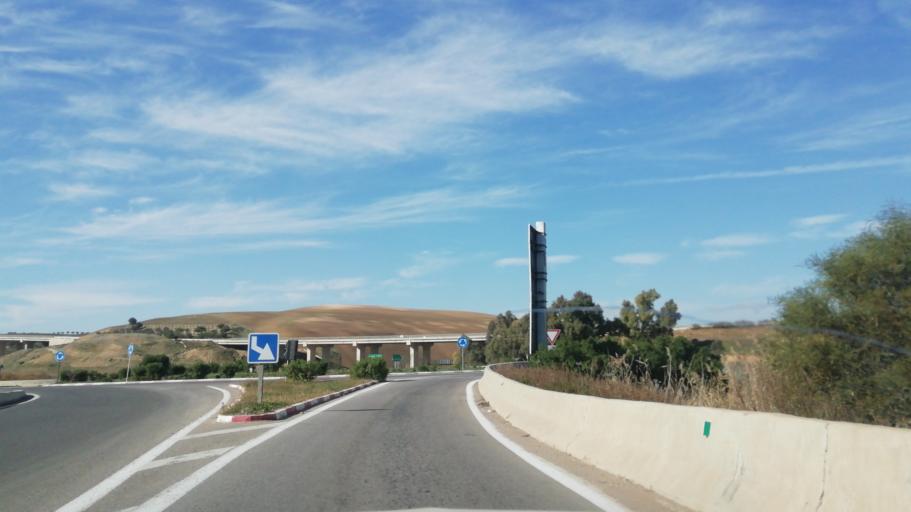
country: DZ
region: Tlemcen
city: Chetouane
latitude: 34.9805
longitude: -1.2367
